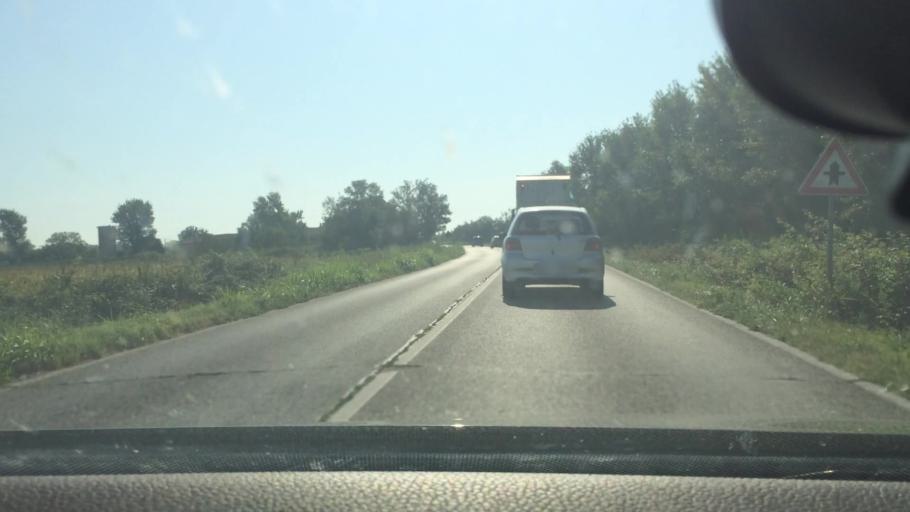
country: IT
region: Emilia-Romagna
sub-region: Provincia di Ferrara
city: Comacchio
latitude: 44.6893
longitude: 12.2083
